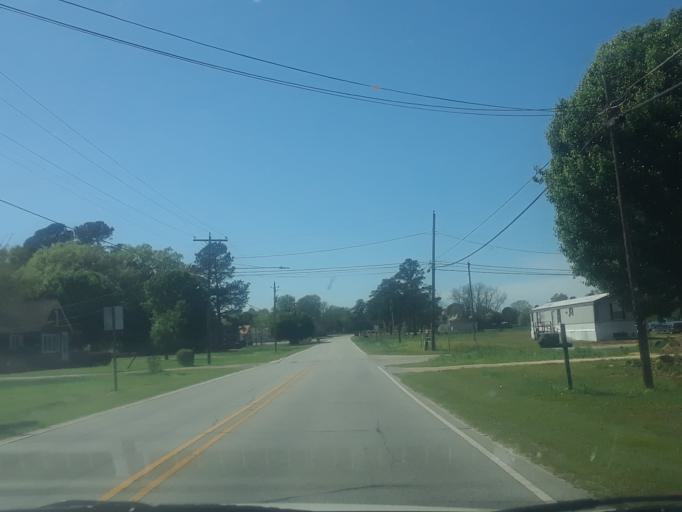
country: US
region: North Carolina
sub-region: Harnett County
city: Erwin
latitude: 35.3177
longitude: -78.6504
